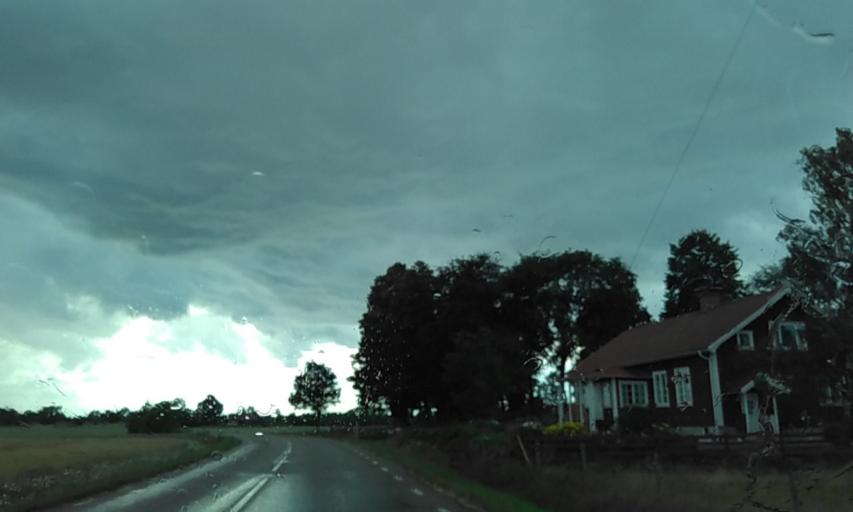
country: SE
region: Vaestra Goetaland
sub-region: Vara Kommun
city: Vara
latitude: 58.4807
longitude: 12.8781
